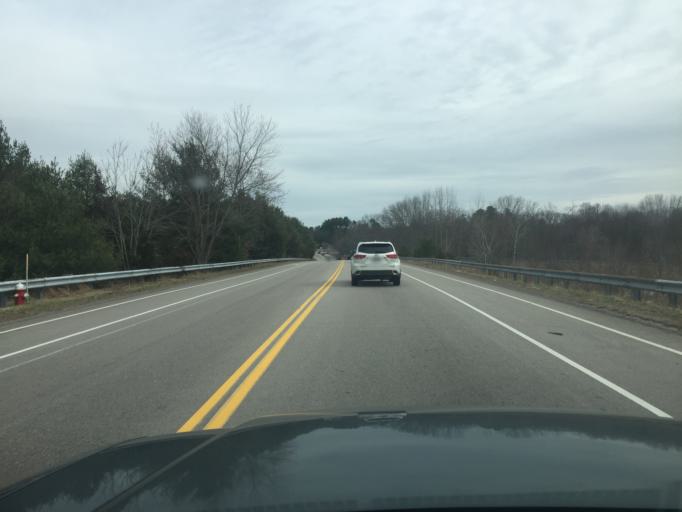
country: US
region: Massachusetts
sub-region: Norfolk County
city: Medfield
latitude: 42.1947
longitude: -71.3283
